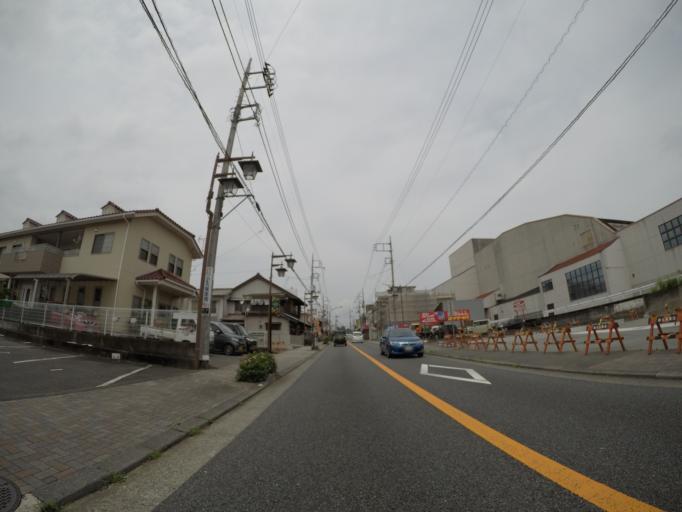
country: JP
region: Shizuoka
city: Fujinomiya
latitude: 35.2269
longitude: 138.6069
